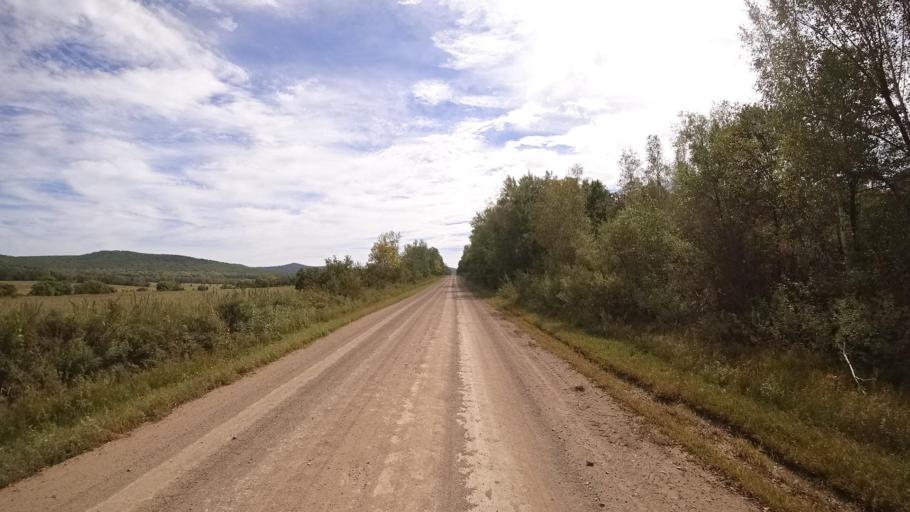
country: RU
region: Primorskiy
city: Yakovlevka
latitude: 44.6120
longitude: 133.5994
